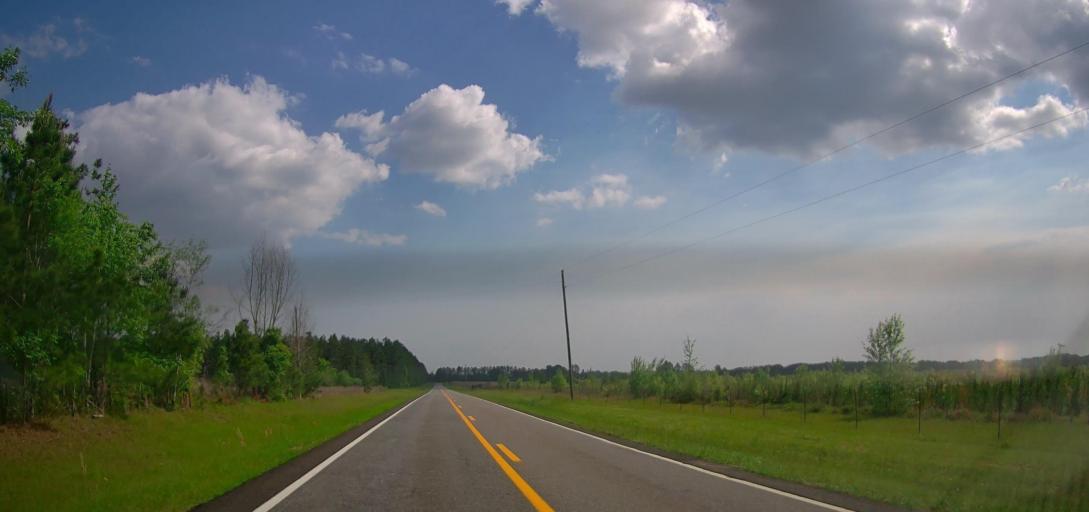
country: US
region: Georgia
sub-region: Laurens County
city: East Dublin
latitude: 32.6440
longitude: -82.8951
